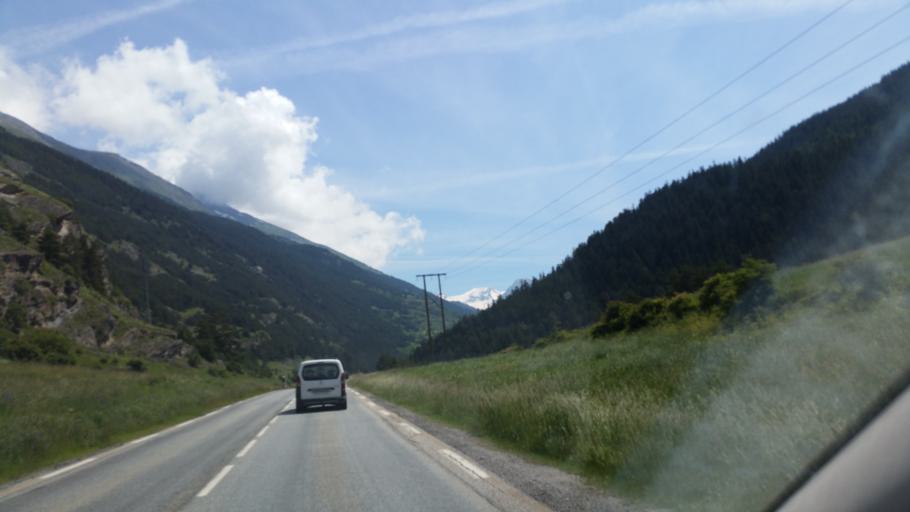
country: FR
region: Rhone-Alpes
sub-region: Departement de la Savoie
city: Modane
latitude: 45.2812
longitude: 6.8243
